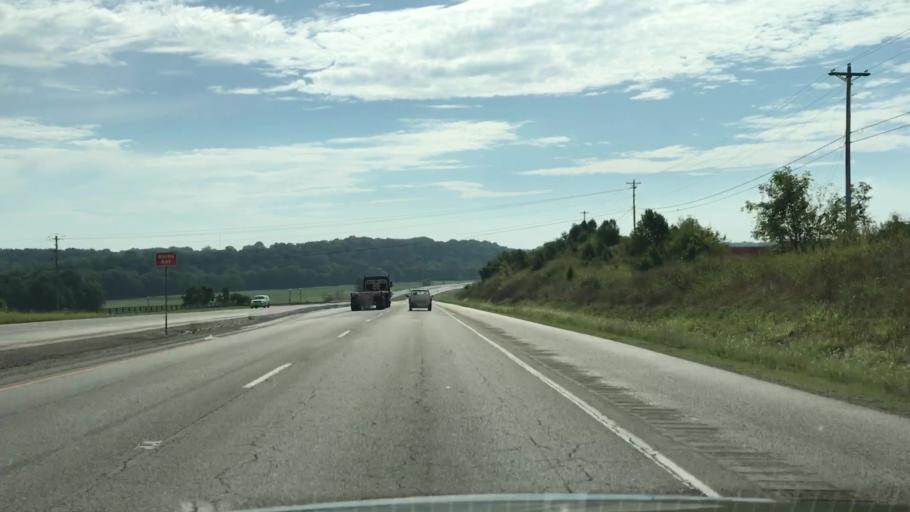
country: US
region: Kentucky
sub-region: Warren County
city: Plano
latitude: 36.9017
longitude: -86.3932
